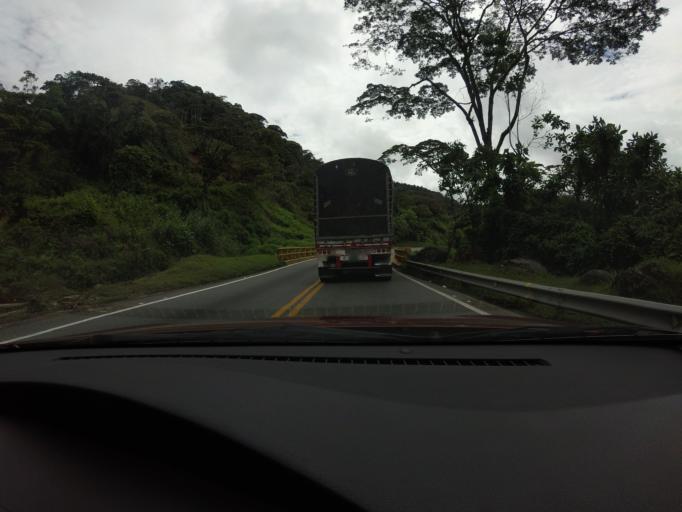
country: CO
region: Antioquia
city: Cocorna
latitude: 6.0816
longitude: -75.2250
